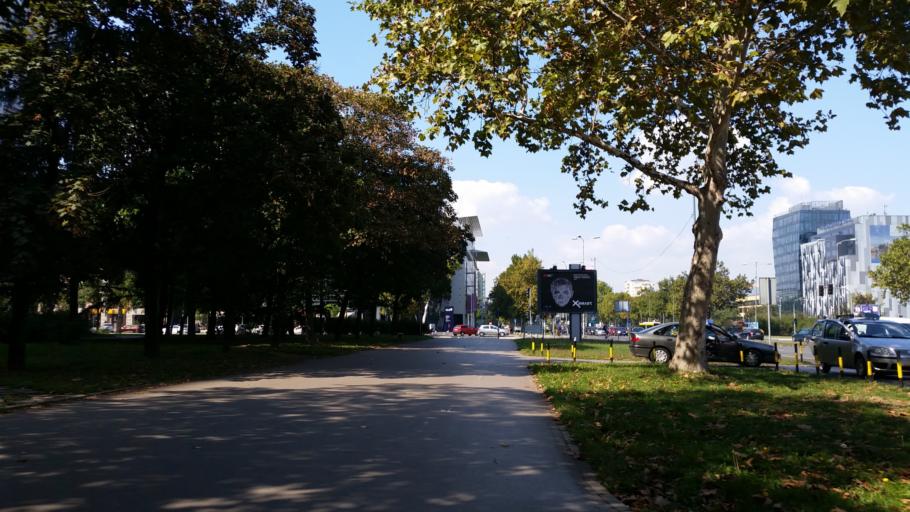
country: RS
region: Central Serbia
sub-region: Belgrade
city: Novi Beograd
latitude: 44.8217
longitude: 20.4183
